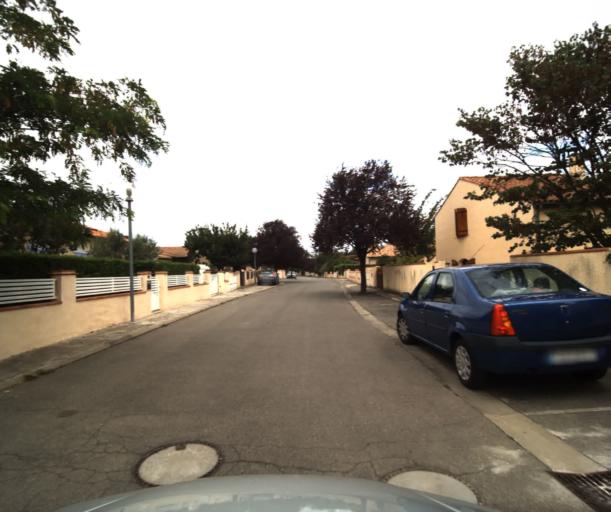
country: FR
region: Midi-Pyrenees
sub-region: Departement de la Haute-Garonne
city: Muret
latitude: 43.4682
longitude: 1.3415
